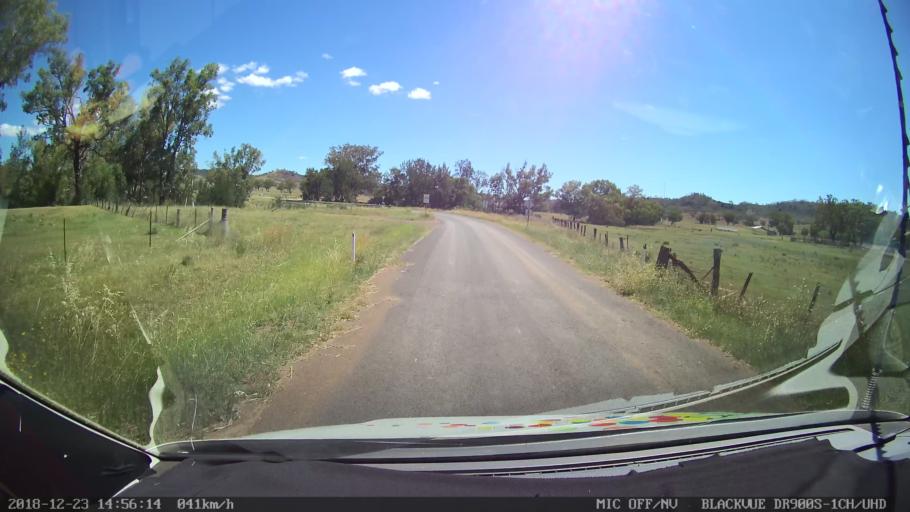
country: AU
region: New South Wales
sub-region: Tamworth Municipality
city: Manilla
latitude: -30.7030
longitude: 150.8303
